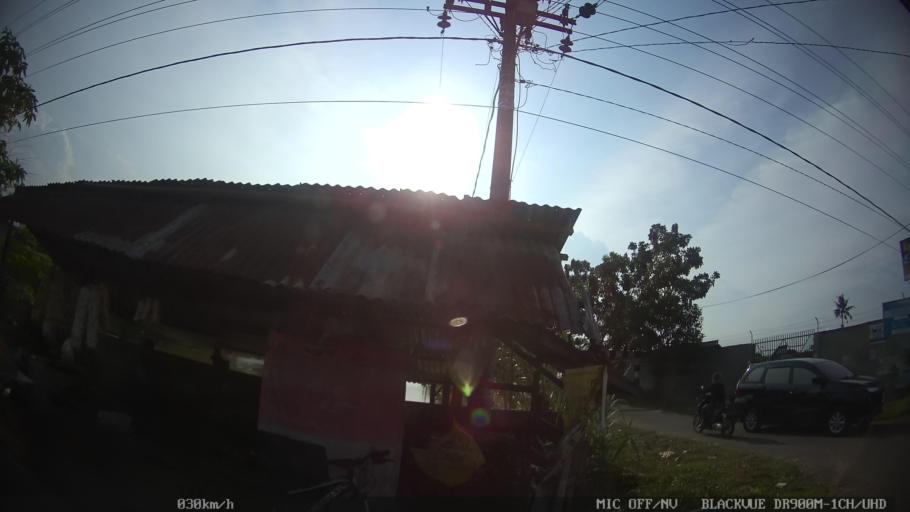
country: ID
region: North Sumatra
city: Binjai
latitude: 3.6204
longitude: 98.5183
